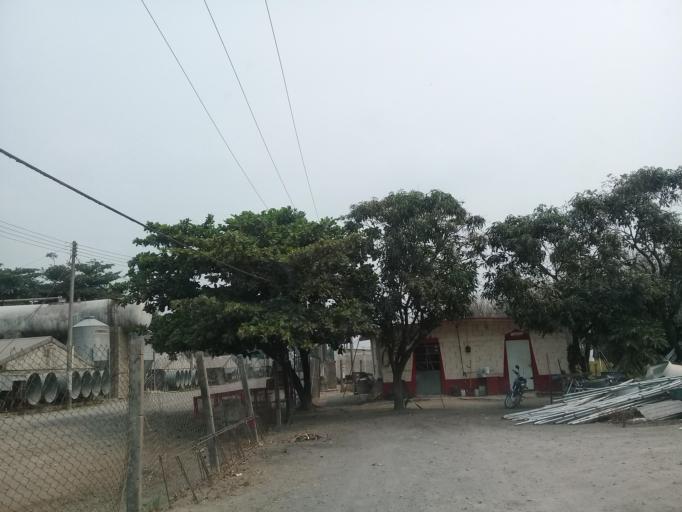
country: MX
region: Veracruz
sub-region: Medellin
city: La Laguna y Monte del Castillo
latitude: 18.9074
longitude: -96.1778
